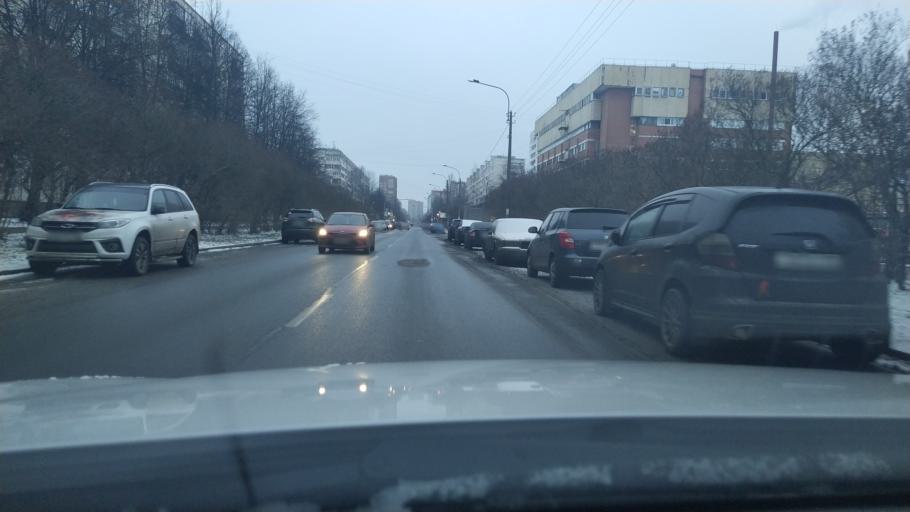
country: RU
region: St.-Petersburg
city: Grazhdanka
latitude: 60.0463
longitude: 30.3924
